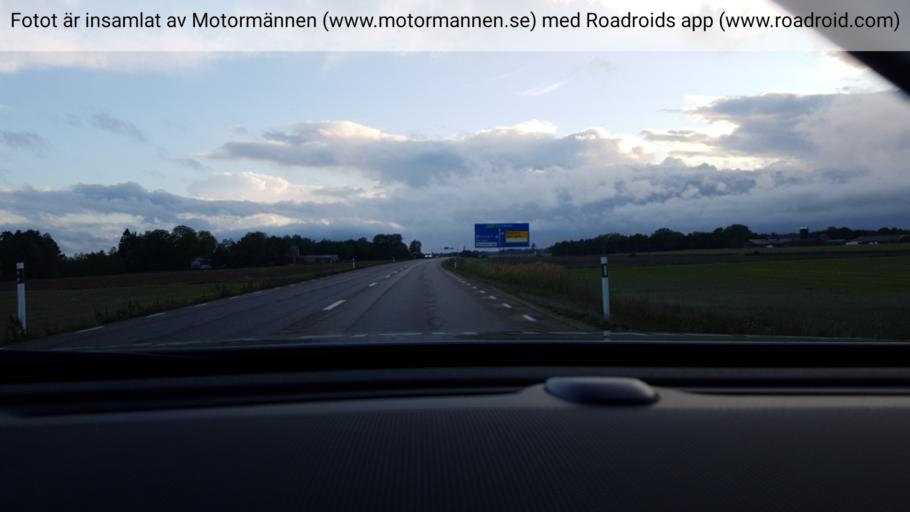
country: SE
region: Vaestra Goetaland
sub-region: Vanersborgs Kommun
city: Bralanda
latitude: 58.5411
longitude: 12.3302
